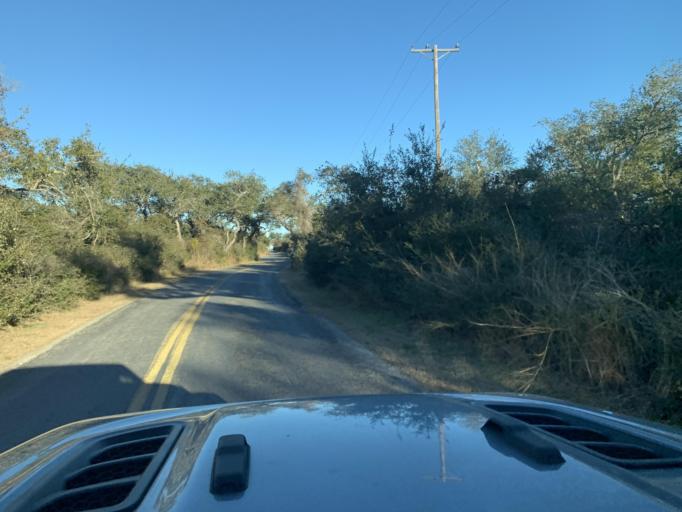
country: US
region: Texas
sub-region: Aransas County
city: Fulton
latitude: 28.1518
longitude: -96.9827
